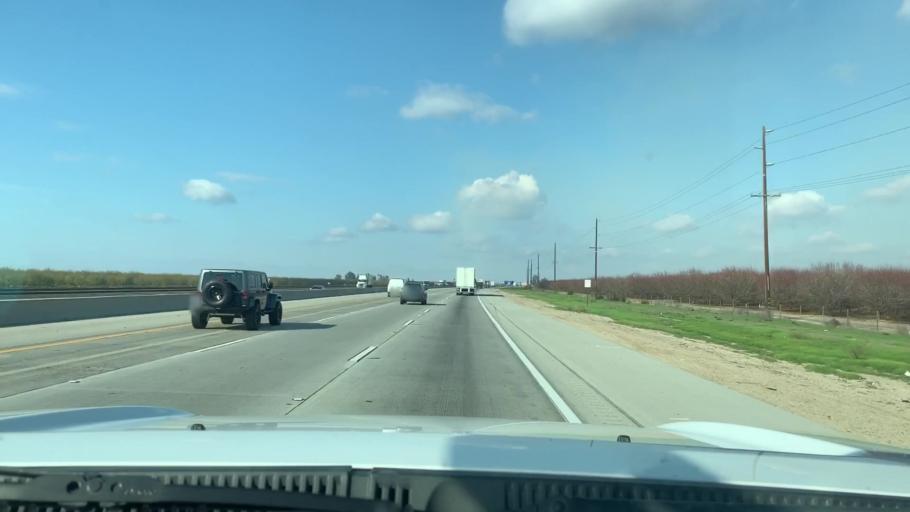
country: US
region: California
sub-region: Kern County
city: Shafter
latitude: 35.5151
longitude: -119.1812
